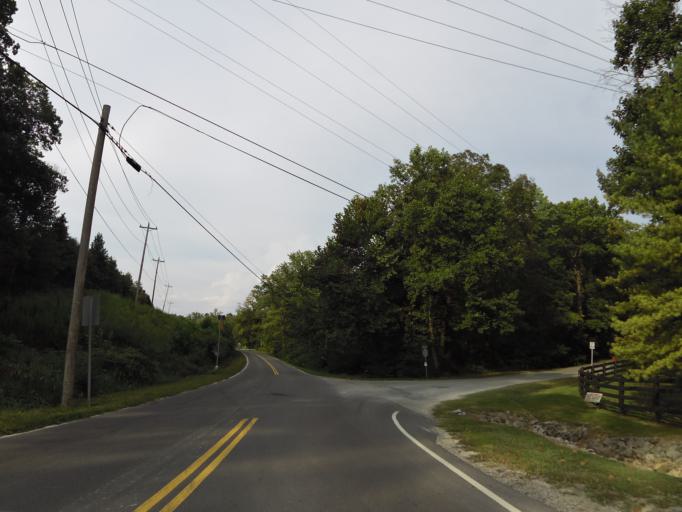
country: US
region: Tennessee
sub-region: Dickson County
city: Burns
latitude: 36.0256
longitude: -87.3300
